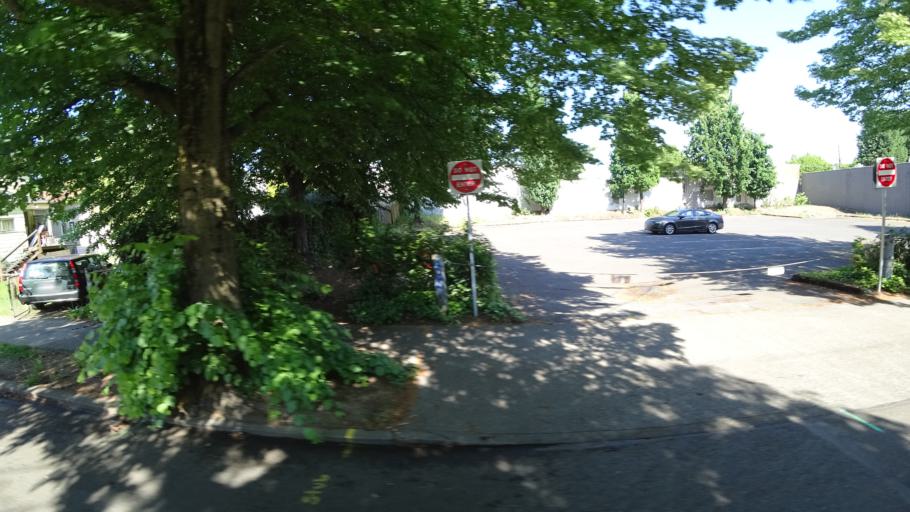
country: US
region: Oregon
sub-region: Multnomah County
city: Portland
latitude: 45.5391
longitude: -122.6687
